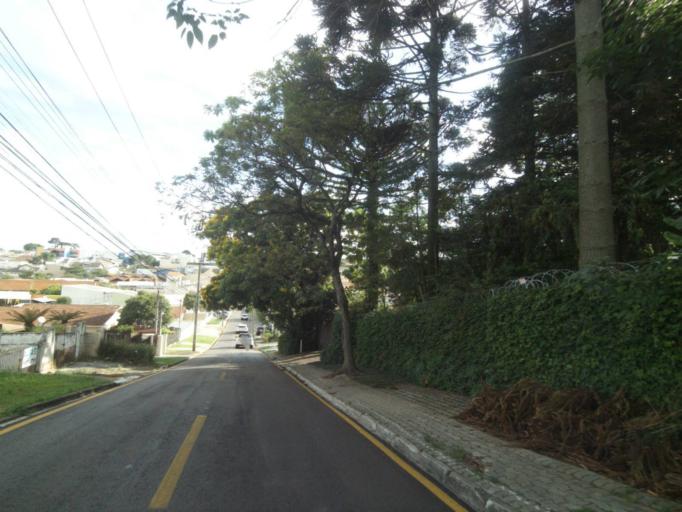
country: BR
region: Parana
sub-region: Curitiba
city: Curitiba
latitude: -25.4444
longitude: -49.3086
